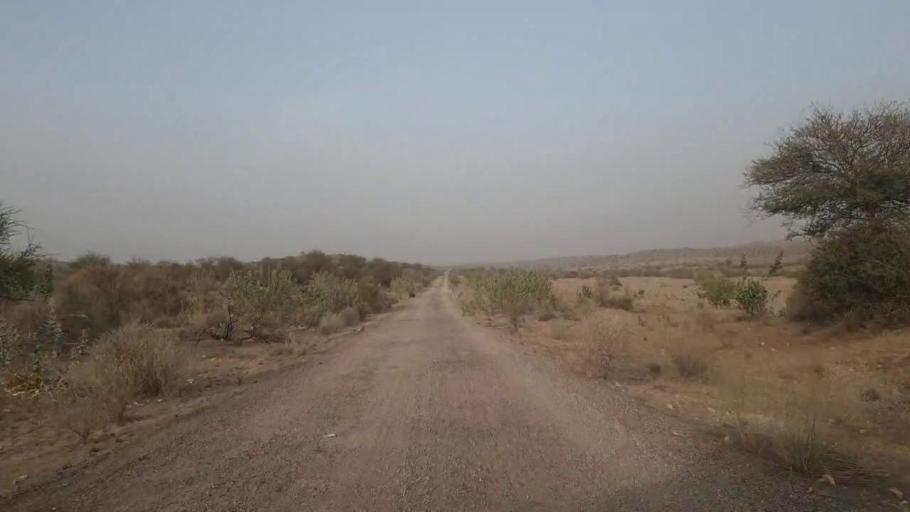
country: PK
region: Sindh
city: Chor
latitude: 25.4944
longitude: 69.9234
